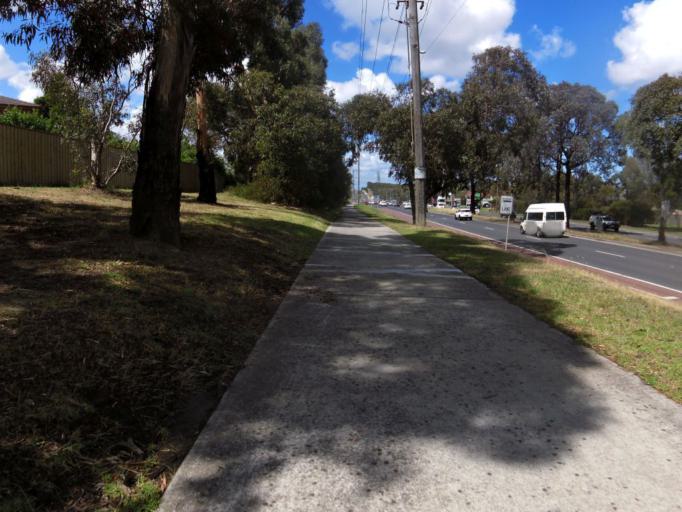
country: AU
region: Victoria
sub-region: Knox
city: Rowville
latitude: -37.9244
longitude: 145.2340
